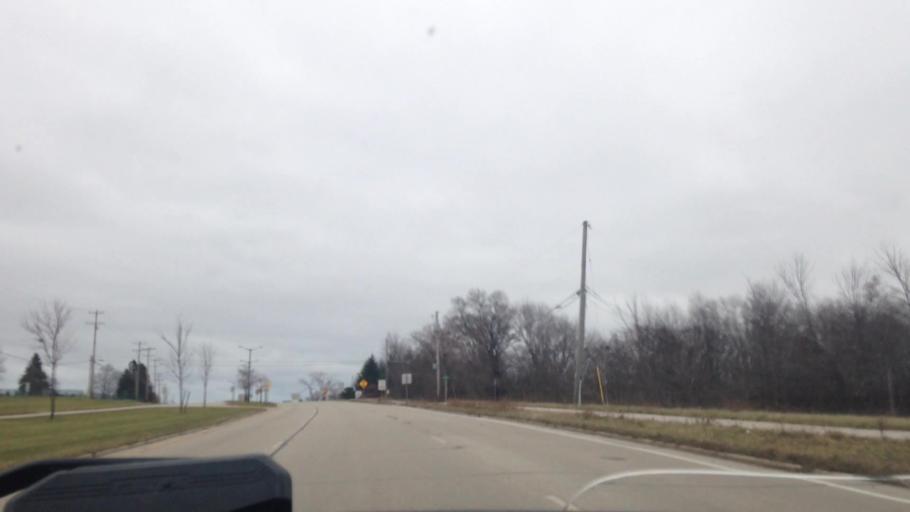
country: US
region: Wisconsin
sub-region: Waukesha County
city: Menomonee Falls
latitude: 43.1773
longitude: -88.0807
